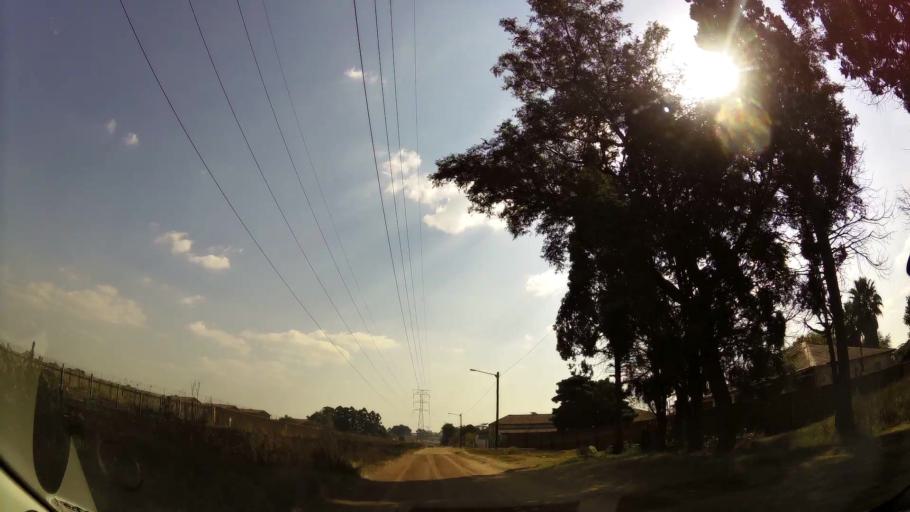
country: ZA
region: Gauteng
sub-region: Ekurhuleni Metropolitan Municipality
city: Benoni
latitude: -26.1396
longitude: 28.3959
